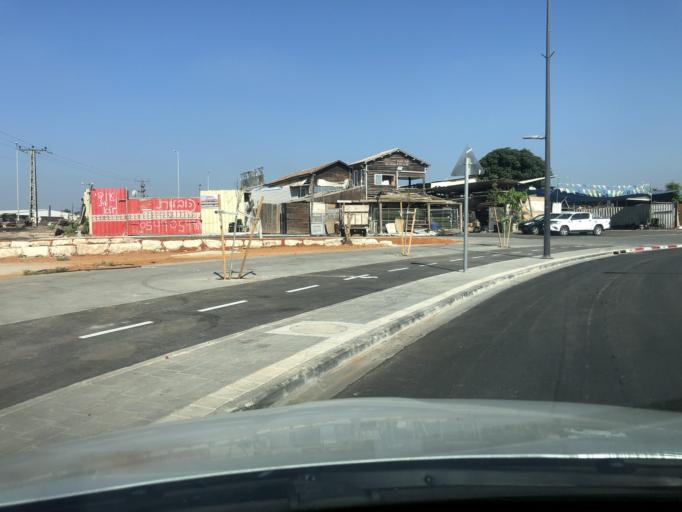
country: IL
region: Central District
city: Jaljulya
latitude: 32.1512
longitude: 34.9490
